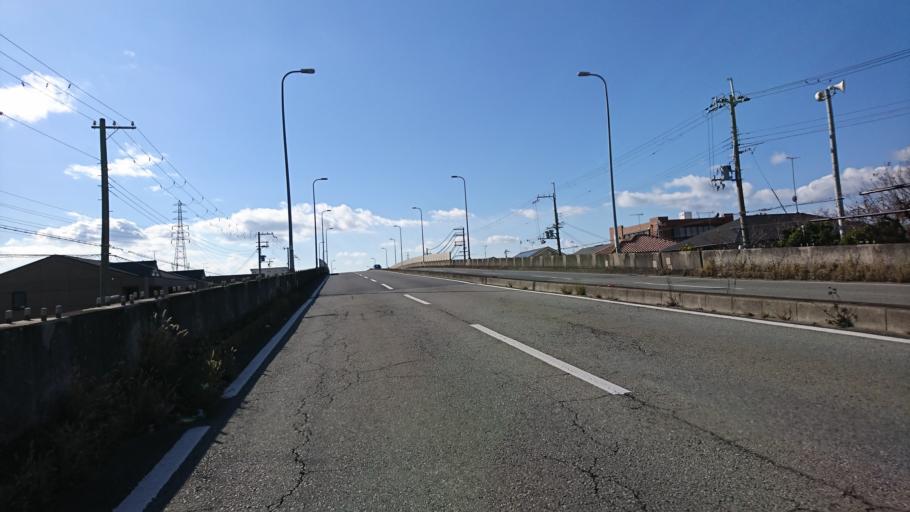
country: JP
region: Hyogo
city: Kakogawacho-honmachi
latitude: 34.7509
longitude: 134.8199
